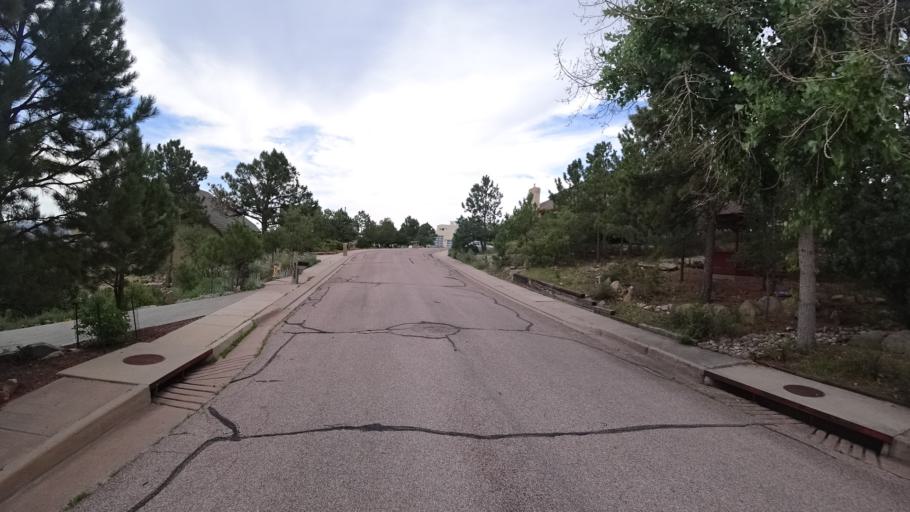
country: US
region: Colorado
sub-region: El Paso County
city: Colorado Springs
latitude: 38.9042
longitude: -104.8476
